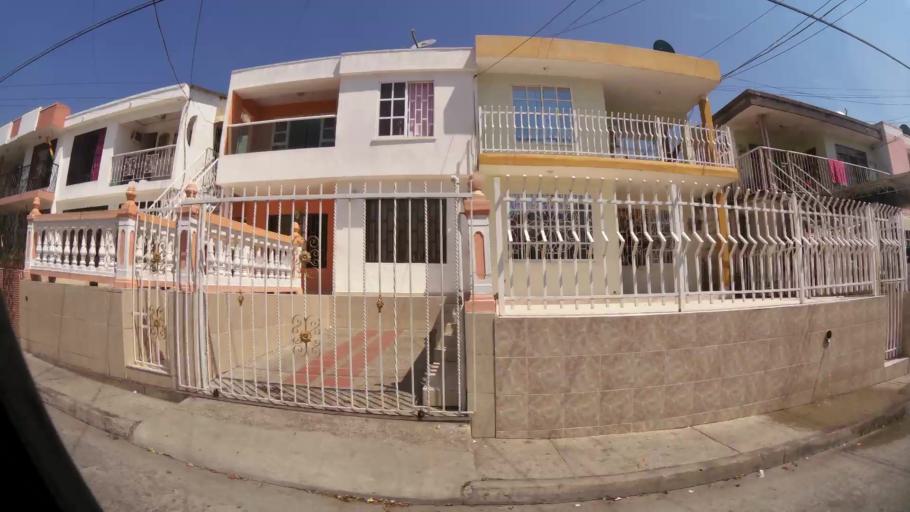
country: CO
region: Bolivar
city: Cartagena
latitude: 10.3983
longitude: -75.4875
